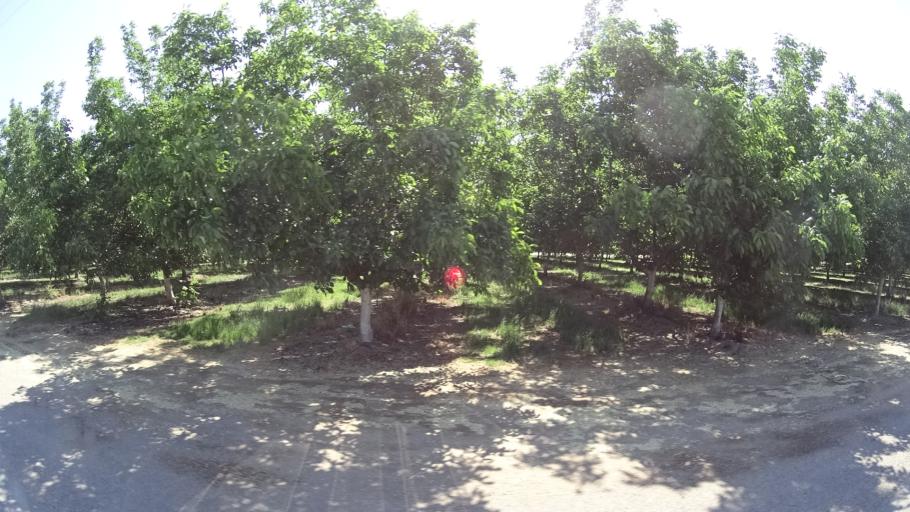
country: US
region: California
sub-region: Kings County
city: Hanford
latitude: 36.3661
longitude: -119.5830
